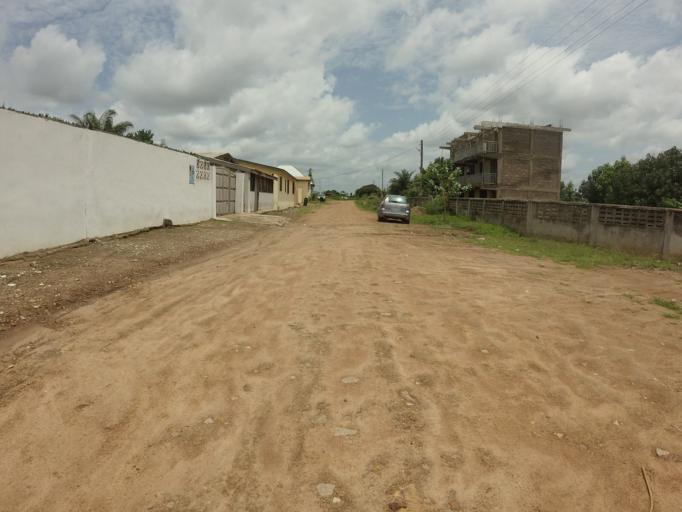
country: GH
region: Volta
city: Ho
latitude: 6.5776
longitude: 0.4614
